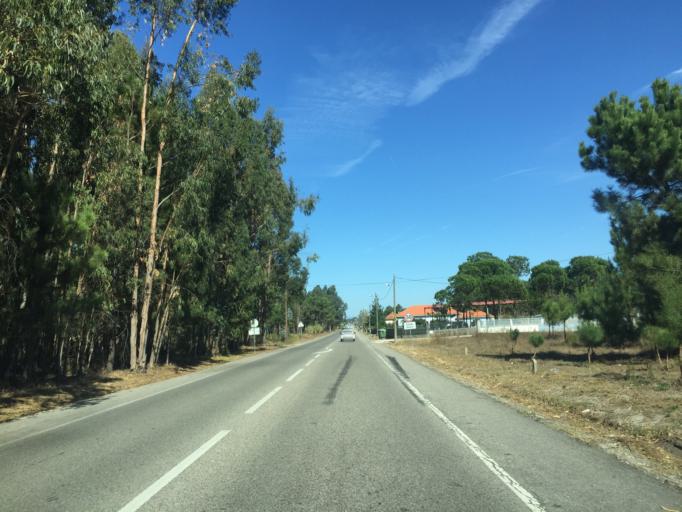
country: PT
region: Coimbra
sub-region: Figueira da Foz
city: Alhadas
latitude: 40.2221
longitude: -8.8066
